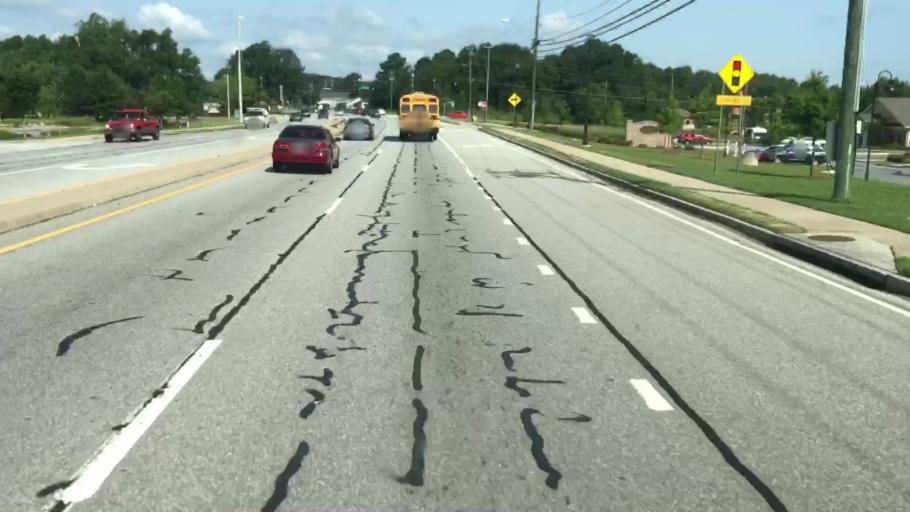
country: US
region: Georgia
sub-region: Gwinnett County
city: Grayson
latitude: 33.8902
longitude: -83.9489
